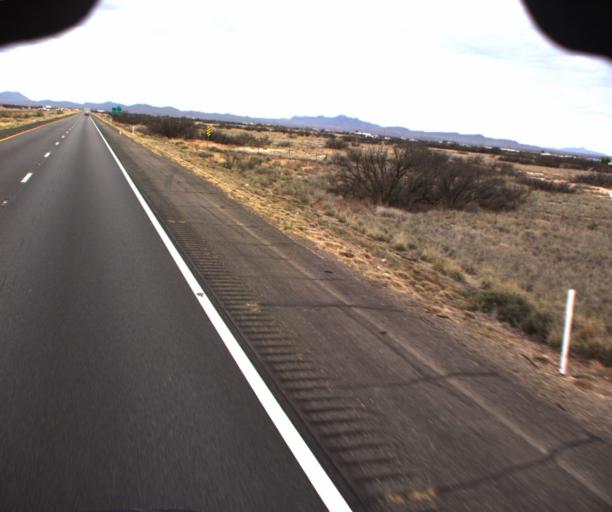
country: US
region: Arizona
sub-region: Cochise County
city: Willcox
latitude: 32.2431
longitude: -109.8623
